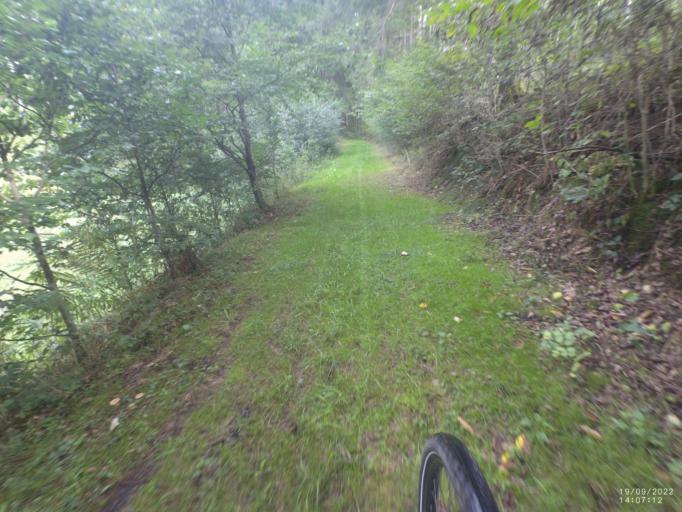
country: DE
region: Rheinland-Pfalz
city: Schutz
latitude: 50.1258
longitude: 6.7659
